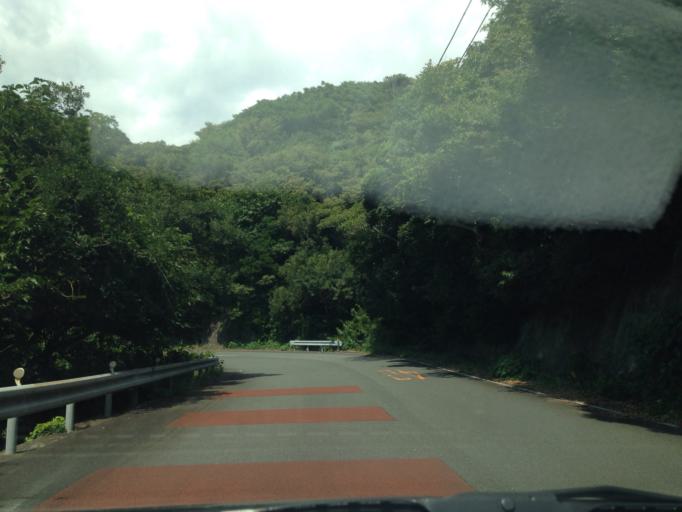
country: JP
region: Shizuoka
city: Shimoda
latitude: 34.6327
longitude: 138.8166
